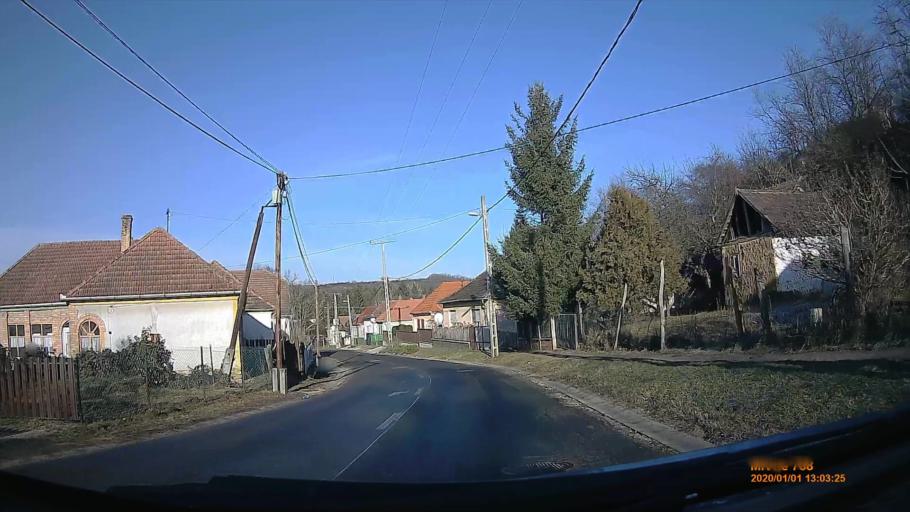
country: HU
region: Heves
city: Parad
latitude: 47.9412
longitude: 20.0232
